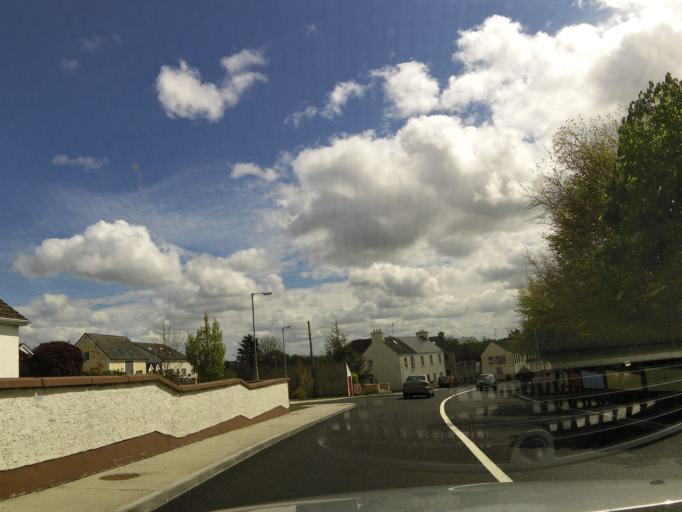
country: IE
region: Connaught
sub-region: County Galway
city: Tuam
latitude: 53.6149
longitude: -8.9004
